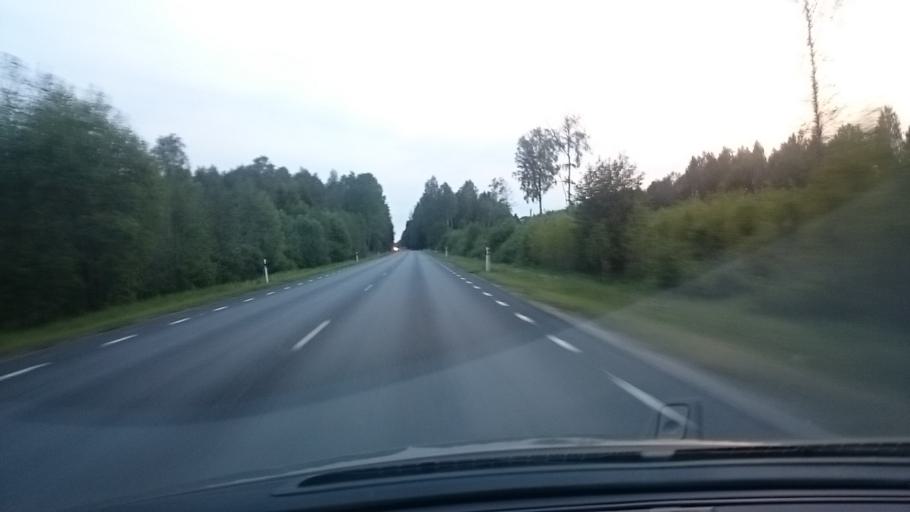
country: EE
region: Raplamaa
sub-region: Kehtna vald
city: Kehtna
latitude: 58.8443
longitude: 25.0512
